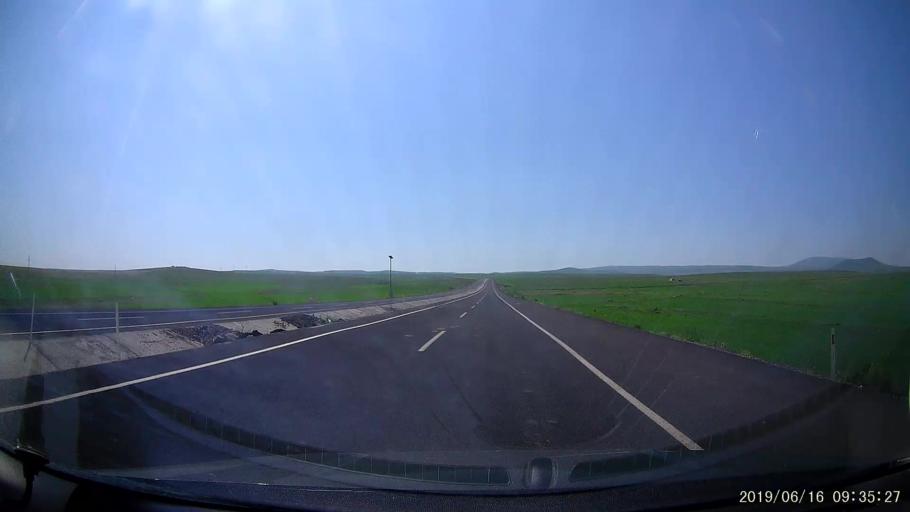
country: TR
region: Kars
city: Kars
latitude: 40.5718
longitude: 43.1561
